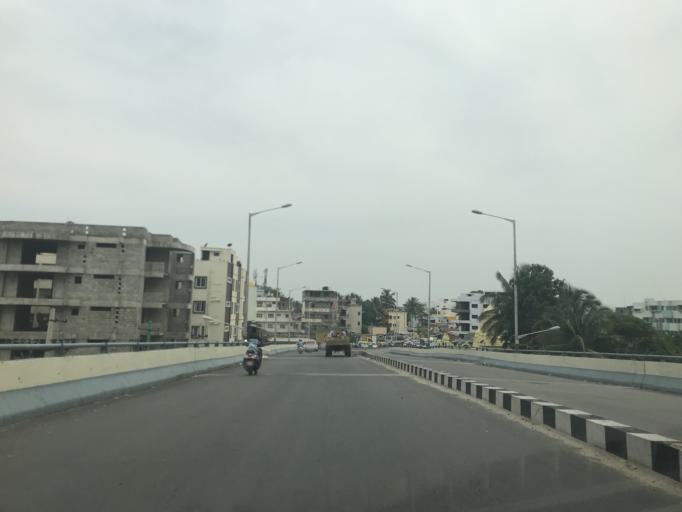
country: IN
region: Karnataka
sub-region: Bangalore Urban
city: Bangalore
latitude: 13.0243
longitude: 77.6313
